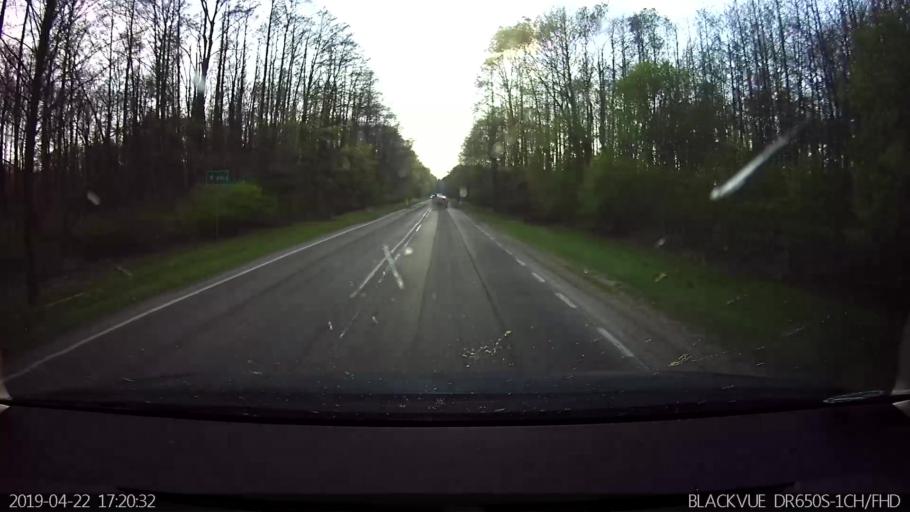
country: PL
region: Masovian Voivodeship
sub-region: Powiat sokolowski
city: Repki
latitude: 52.3887
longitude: 22.3808
